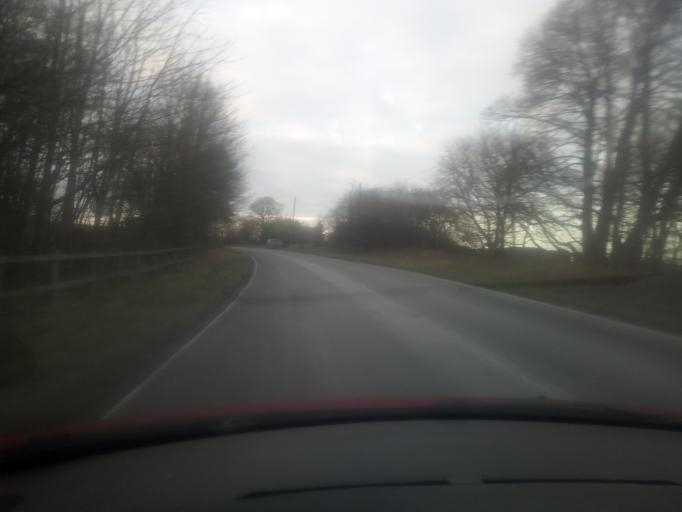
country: GB
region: England
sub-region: Northumberland
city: Healey
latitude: 54.9172
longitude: -1.9540
